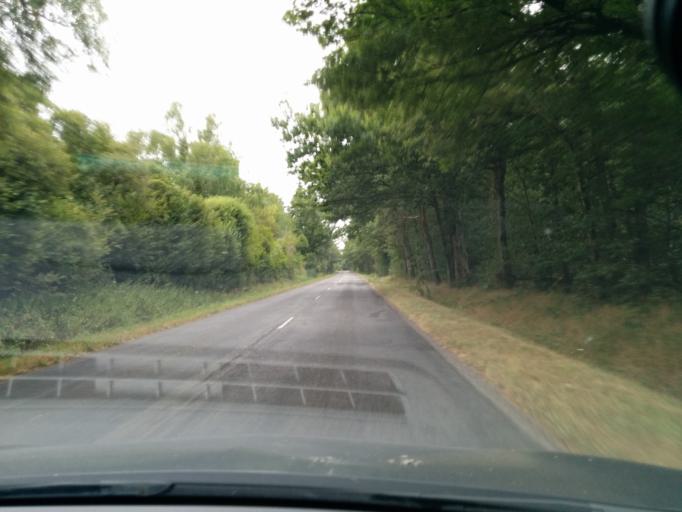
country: FR
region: Centre
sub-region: Departement du Loiret
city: Chateauneuf-sur-Loire
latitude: 47.8822
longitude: 2.1992
